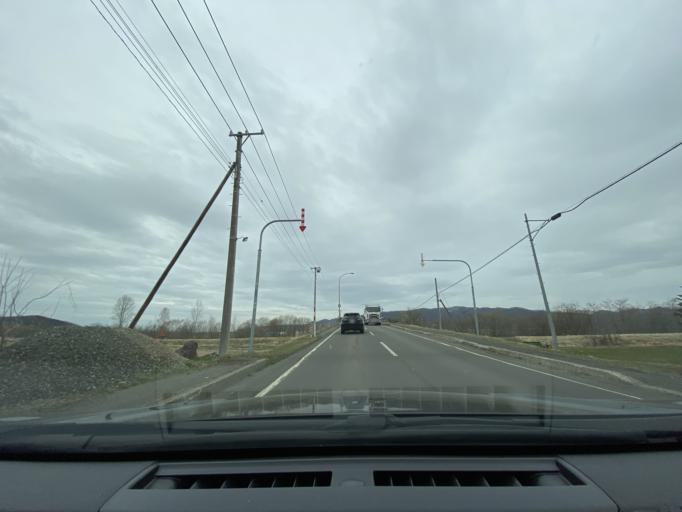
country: JP
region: Hokkaido
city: Nayoro
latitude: 44.1124
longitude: 142.4795
